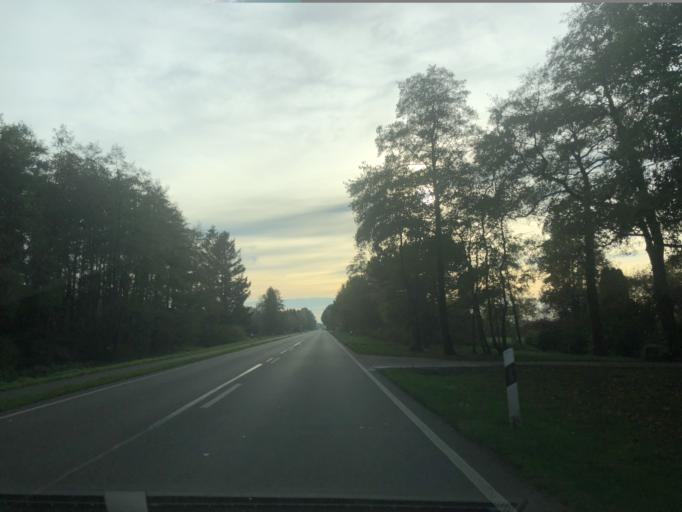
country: DE
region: Lower Saxony
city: Edewecht
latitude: 53.0794
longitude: 7.9326
